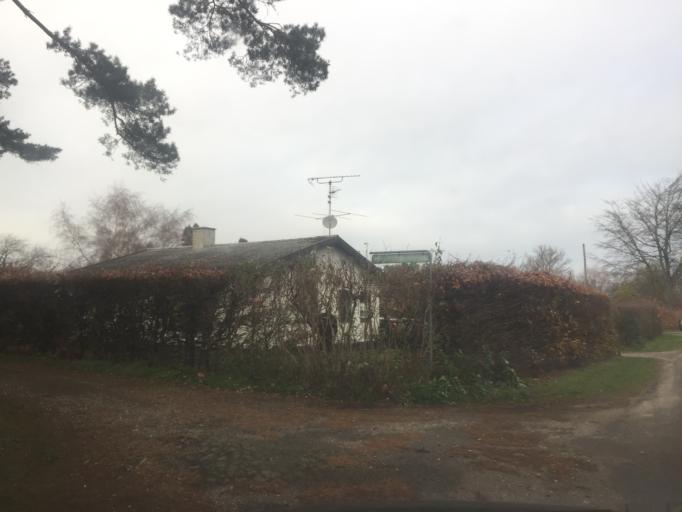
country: DK
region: Capital Region
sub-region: Halsnaes Kommune
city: Liseleje
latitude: 56.0074
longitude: 11.9940
